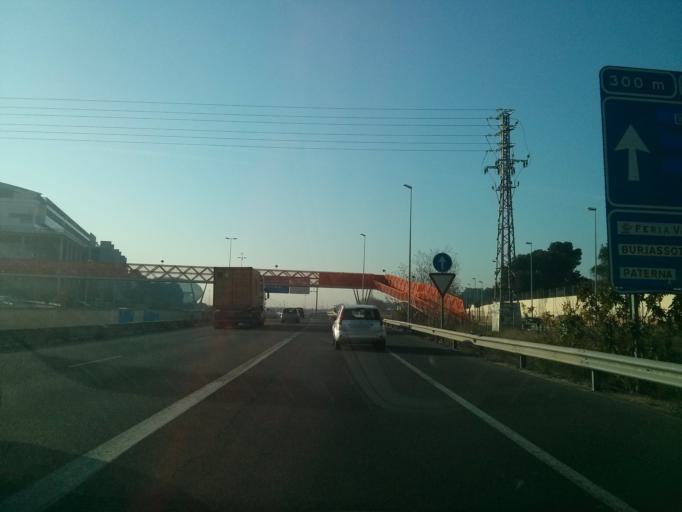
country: ES
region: Valencia
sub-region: Provincia de Valencia
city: Paterna
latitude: 39.5071
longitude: -0.4330
